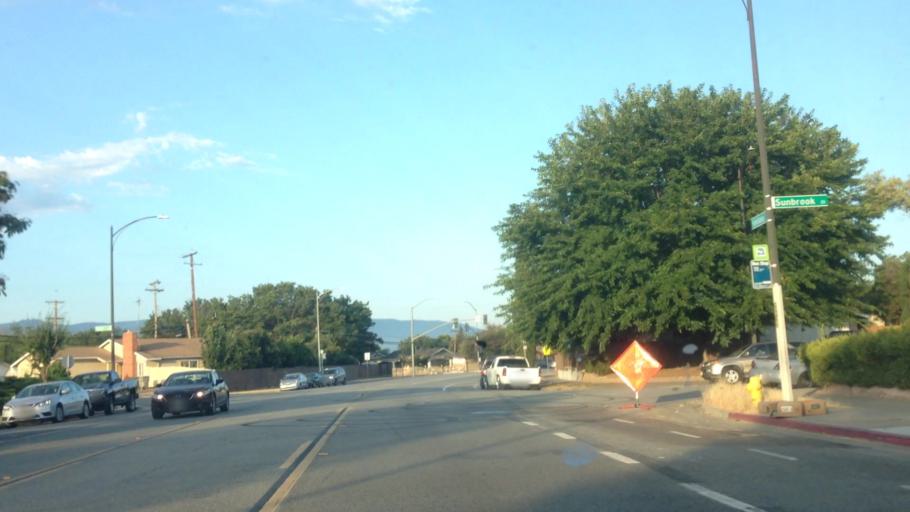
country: US
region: California
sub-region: Santa Clara County
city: Seven Trees
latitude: 37.2888
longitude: -121.8203
